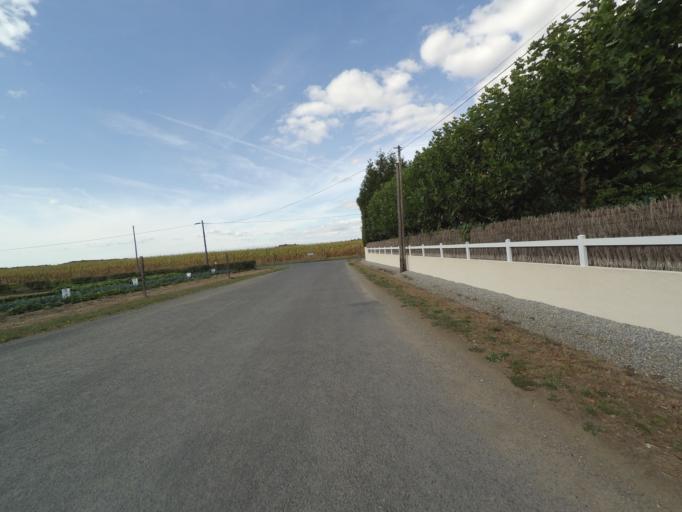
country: FR
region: Pays de la Loire
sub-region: Departement de la Vendee
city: Bouffere
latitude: 46.9835
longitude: -1.3810
